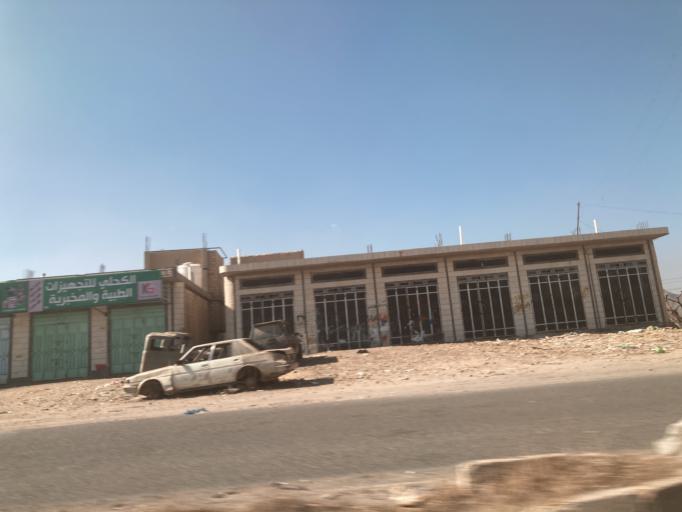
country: YE
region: Ad Dali'
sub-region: Qa'atabah
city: Qa`tabah
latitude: 13.8158
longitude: 44.7167
